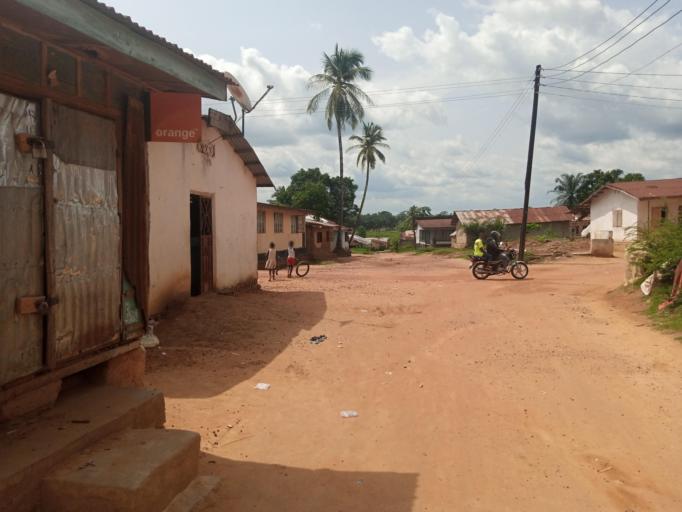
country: SL
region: Southern Province
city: Bo
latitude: 7.9763
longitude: -11.7343
